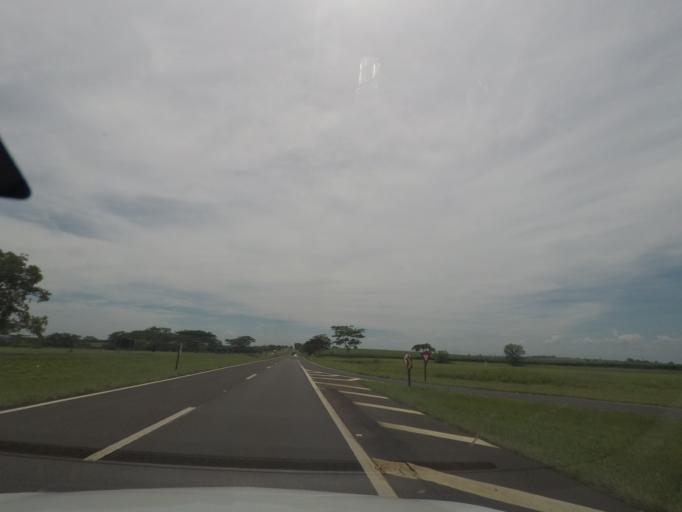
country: BR
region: Sao Paulo
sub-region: Bebedouro
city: Bebedouro
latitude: -20.9623
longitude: -48.4428
